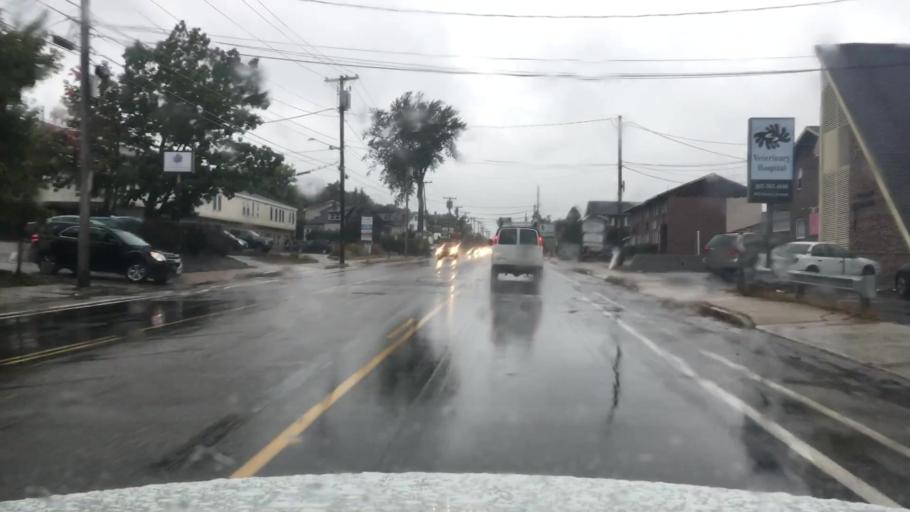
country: US
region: Maine
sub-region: Cumberland County
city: Portland
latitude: 43.6806
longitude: -70.2894
